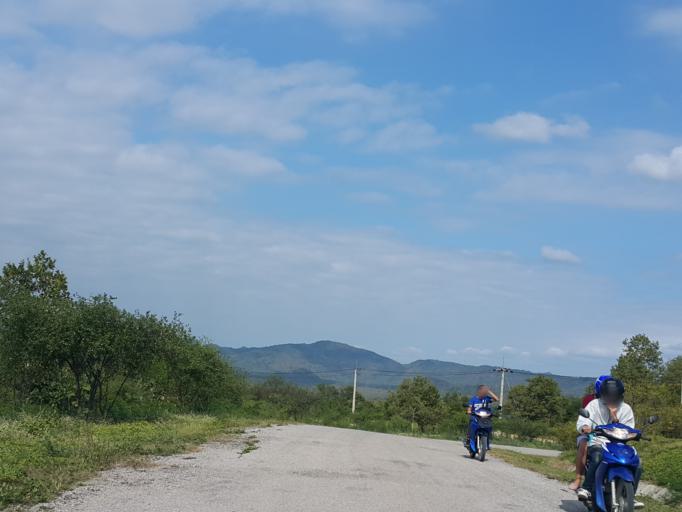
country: TH
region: Lampang
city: Mae Mo
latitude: 18.3509
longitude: 99.7547
